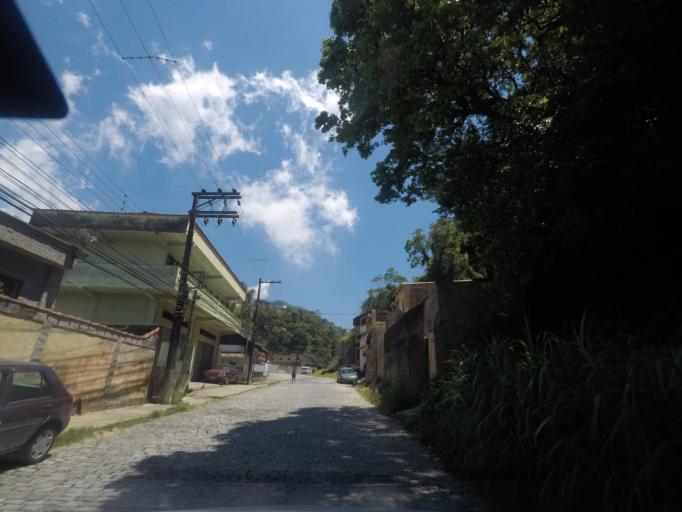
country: BR
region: Rio de Janeiro
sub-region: Petropolis
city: Petropolis
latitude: -22.5321
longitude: -43.1725
